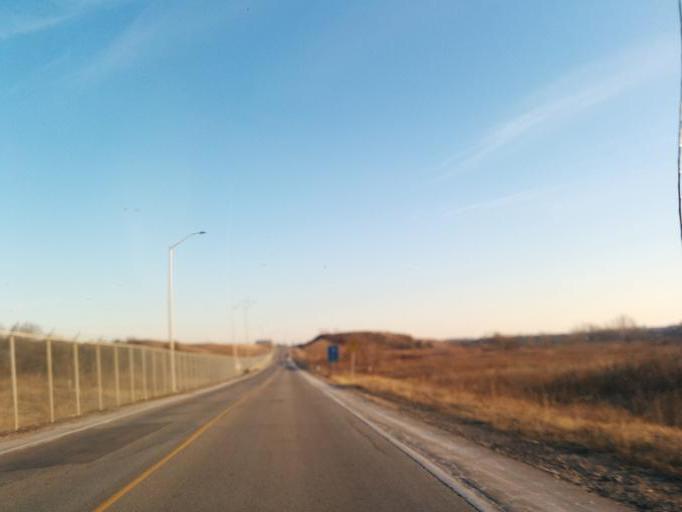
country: CA
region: Ontario
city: Etobicoke
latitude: 43.6730
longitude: -79.6407
